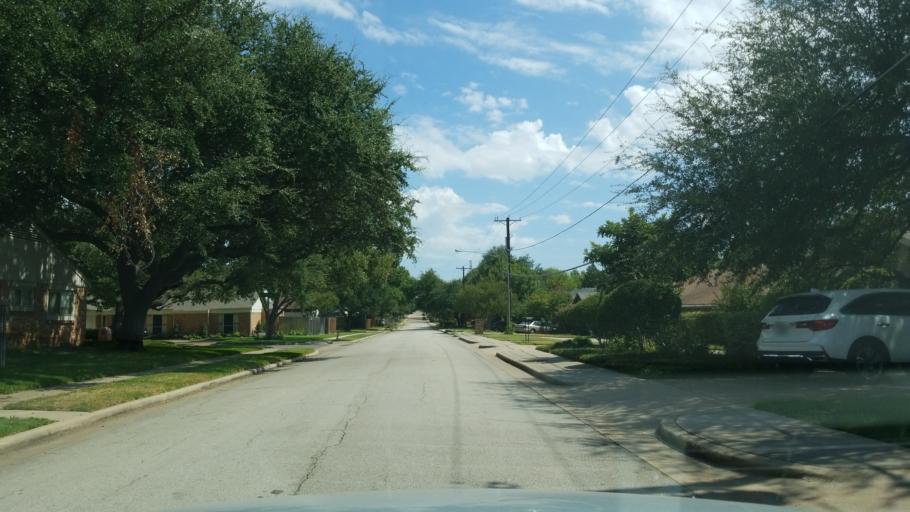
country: US
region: Texas
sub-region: Dallas County
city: Addison
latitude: 32.9596
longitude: -96.7819
